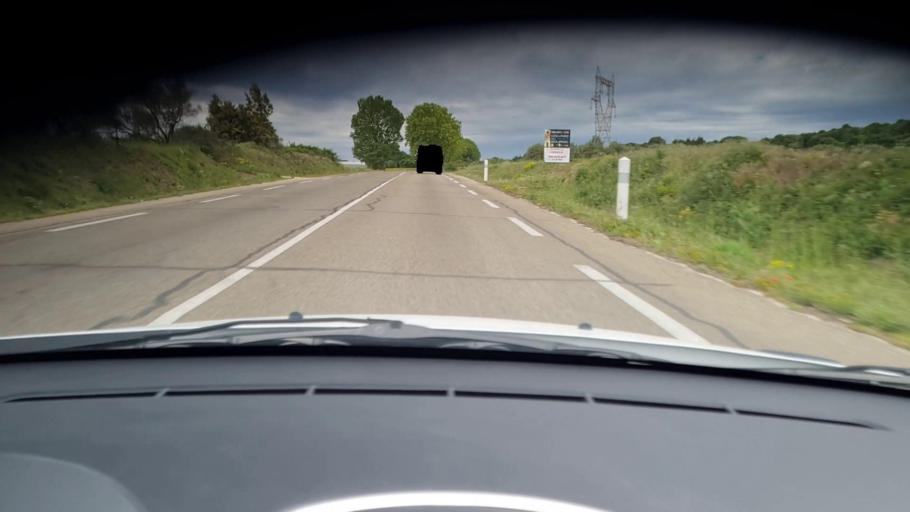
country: FR
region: Languedoc-Roussillon
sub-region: Departement du Gard
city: Uzes
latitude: 43.9812
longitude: 4.4693
